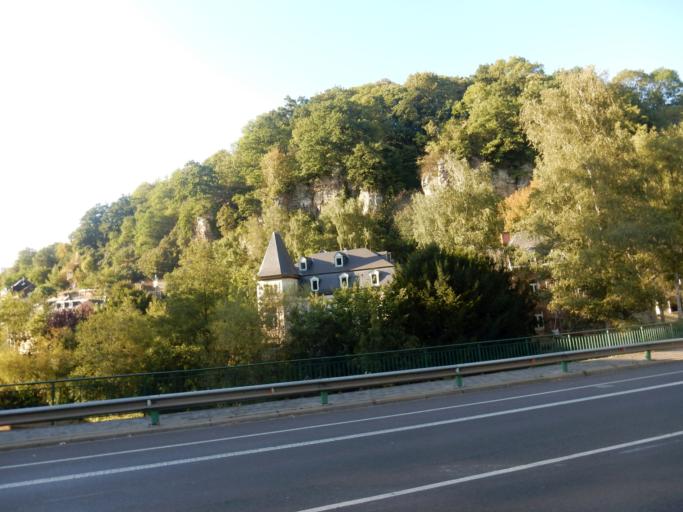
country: LU
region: Luxembourg
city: Kirchberg
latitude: 49.6082
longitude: 6.1501
